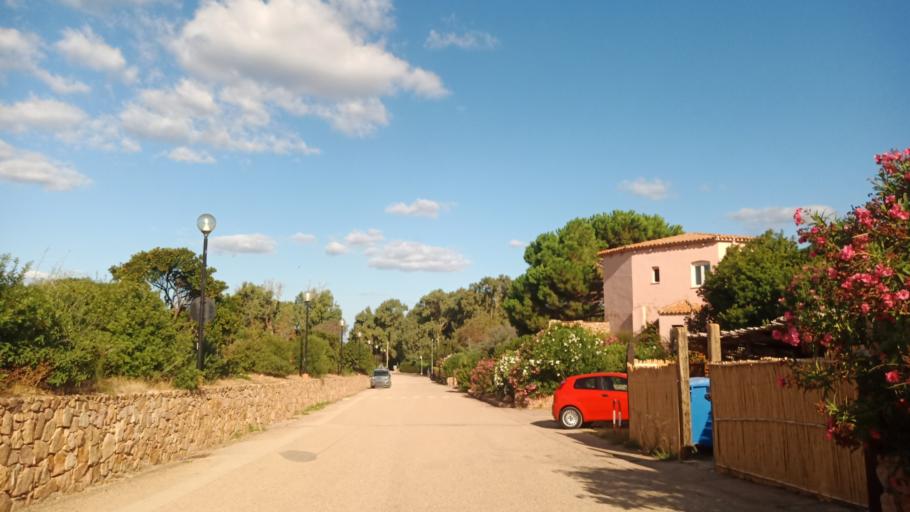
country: IT
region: Sardinia
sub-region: Provincia di Olbia-Tempio
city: Trinita d'Agultu
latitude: 41.0230
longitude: 8.8964
